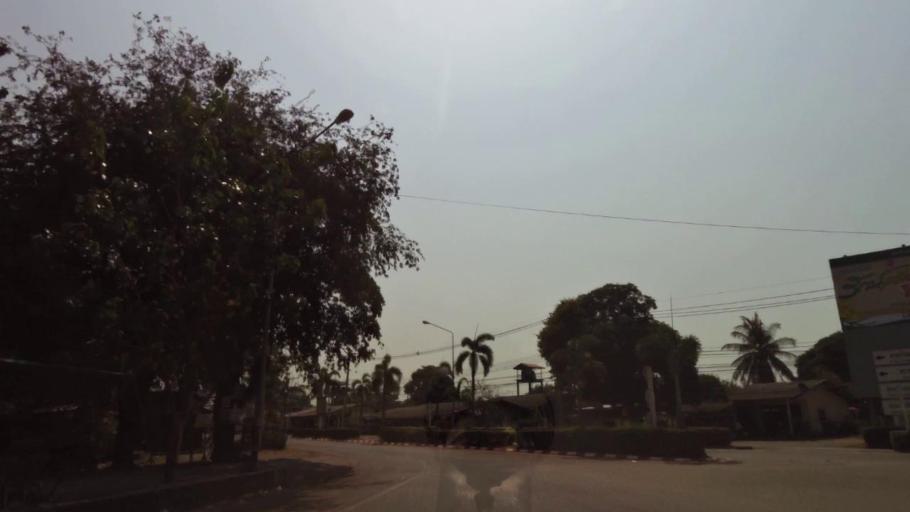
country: TH
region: Chanthaburi
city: Tha Mai
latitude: 12.5618
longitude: 101.9133
